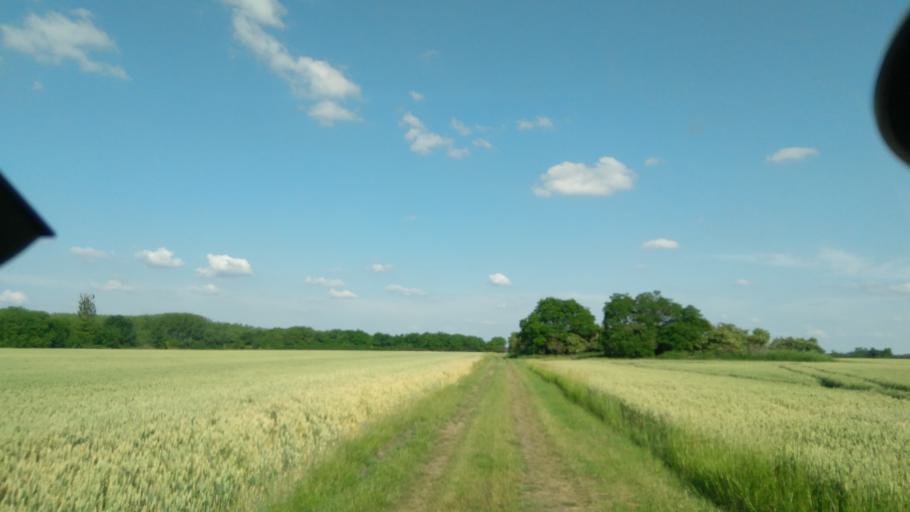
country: HU
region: Bekes
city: Doboz
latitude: 46.6987
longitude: 21.2278
